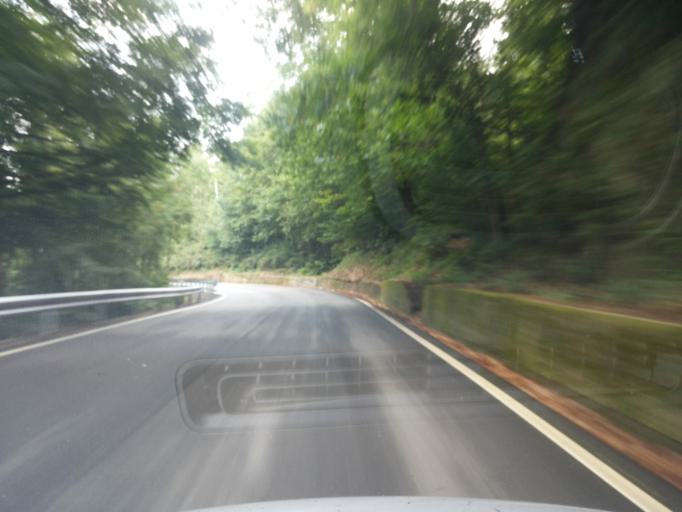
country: IT
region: Piedmont
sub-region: Provincia di Biella
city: Pollone
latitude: 45.6076
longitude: 7.9899
